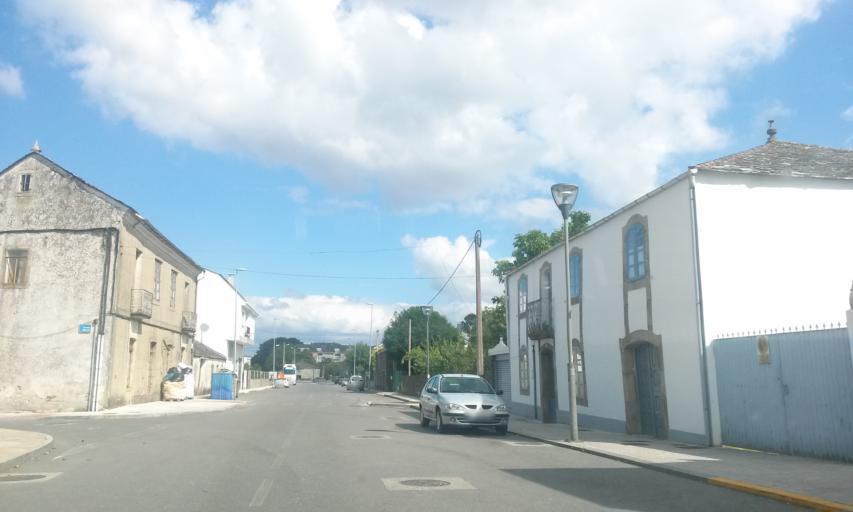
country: ES
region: Galicia
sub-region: Provincia de Lugo
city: Outeiro de Rei
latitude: 43.1017
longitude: -7.6134
